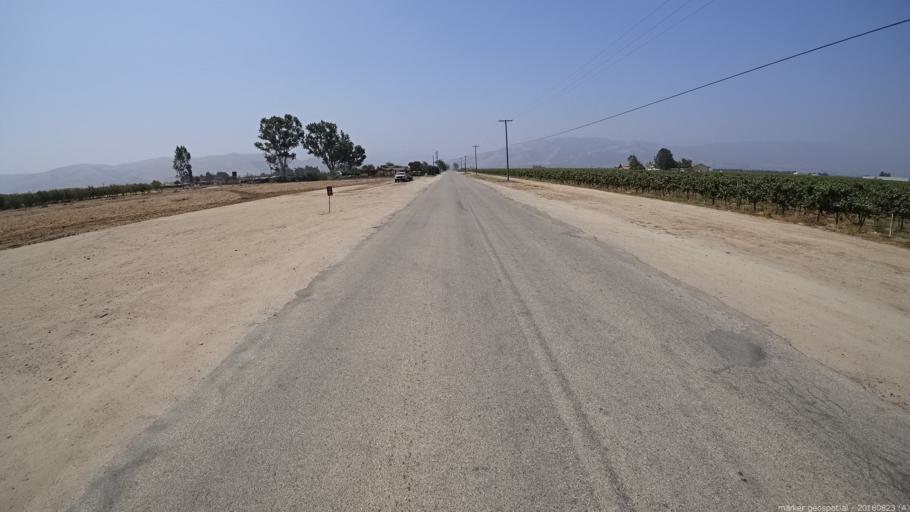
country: US
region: California
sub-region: Monterey County
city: Greenfield
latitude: 36.3223
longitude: -121.2565
